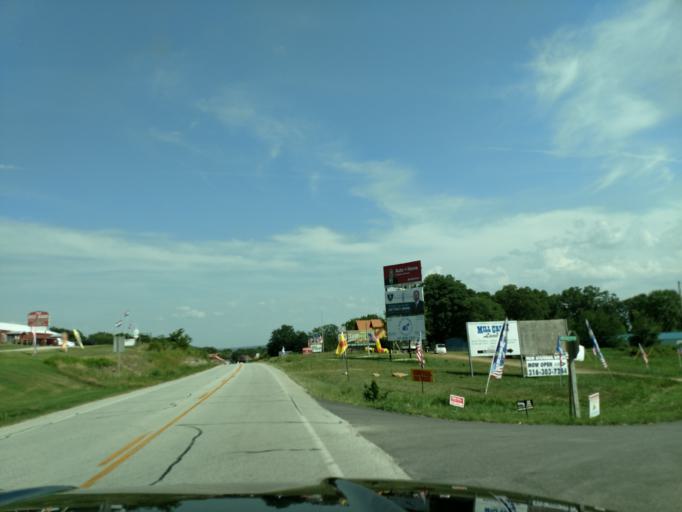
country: US
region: Missouri
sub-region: Barry County
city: Shell Knob
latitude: 36.6239
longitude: -93.6202
